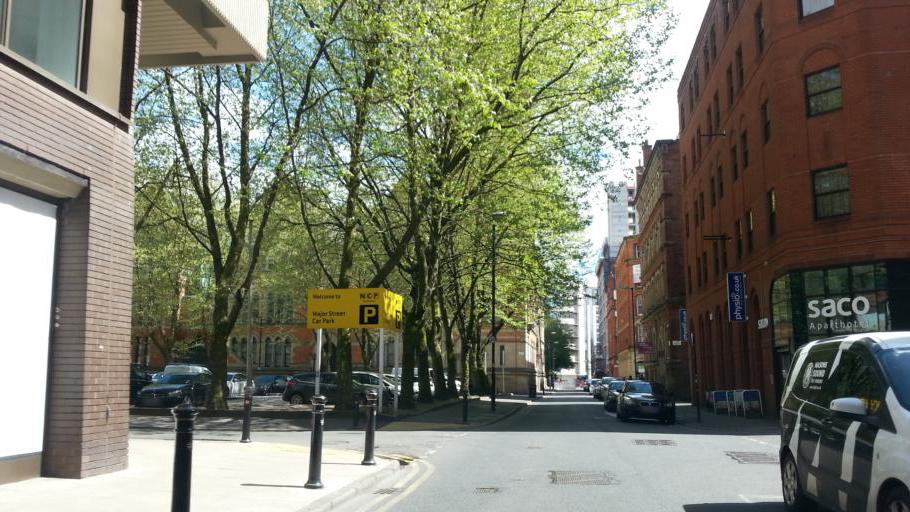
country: GB
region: England
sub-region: Manchester
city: Manchester
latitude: 53.4791
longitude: -2.2364
